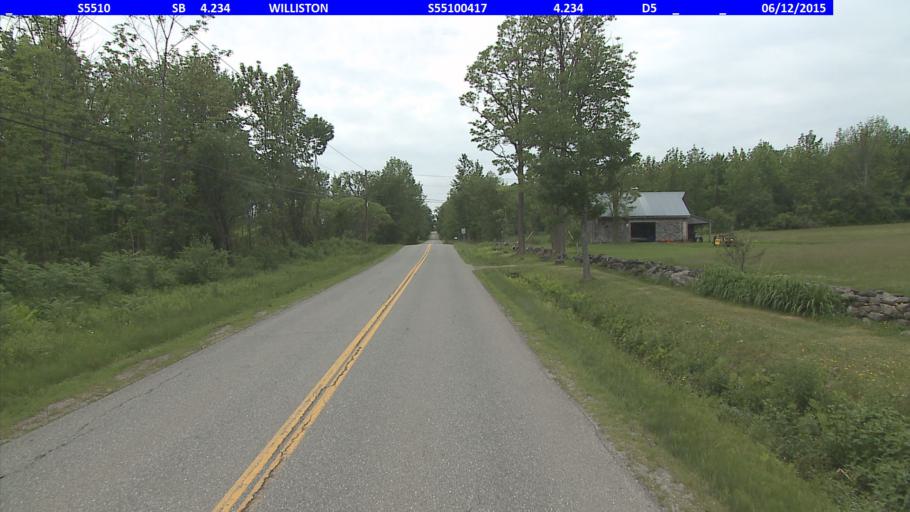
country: US
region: Vermont
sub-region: Chittenden County
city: Williston
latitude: 44.4297
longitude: -73.0743
